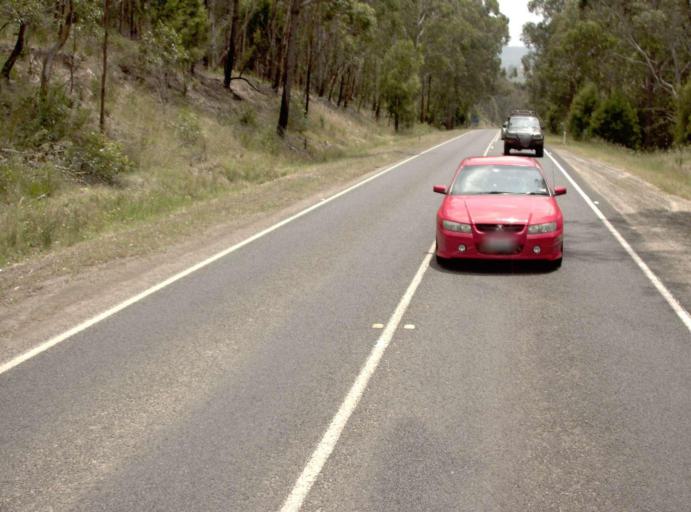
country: AU
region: Victoria
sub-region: Latrobe
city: Traralgon
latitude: -38.4446
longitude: 146.7340
